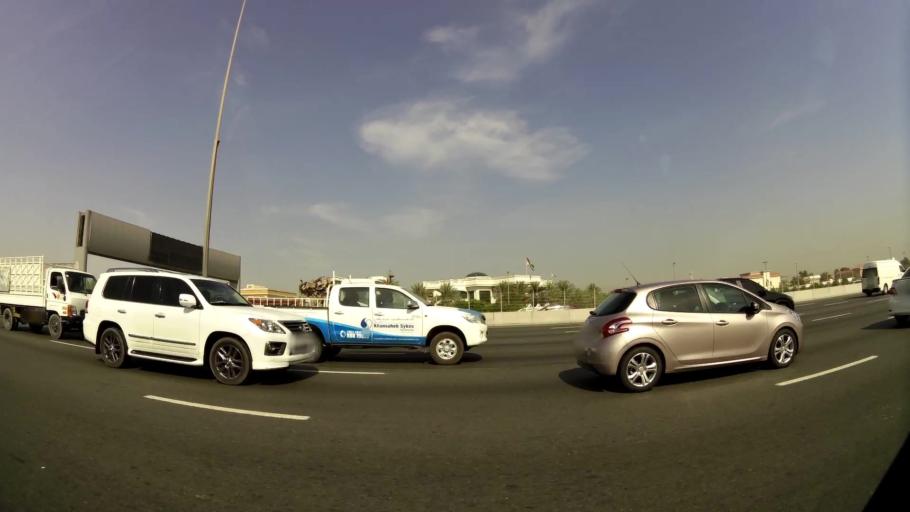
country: AE
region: Ash Shariqah
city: Sharjah
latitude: 25.2438
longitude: 55.4050
